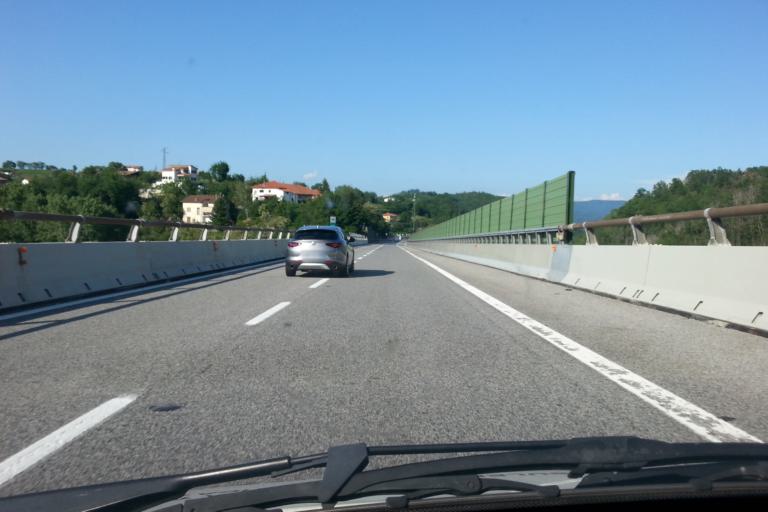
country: IT
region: Liguria
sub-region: Provincia di Savona
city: Cosseria
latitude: 44.3616
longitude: 8.2389
